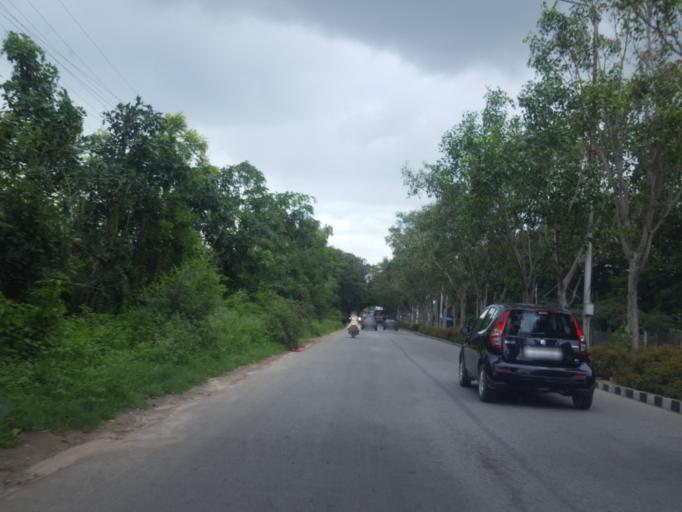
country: IN
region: Telangana
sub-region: Medak
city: Serilingampalle
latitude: 17.4664
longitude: 78.3327
